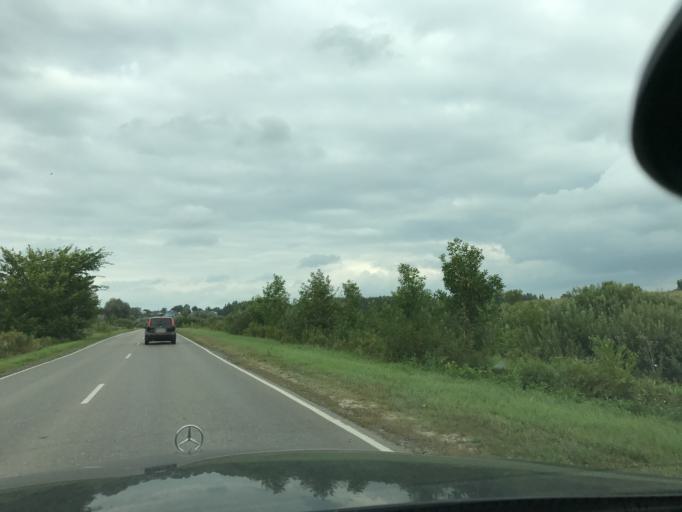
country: RU
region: Nizjnij Novgorod
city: Pavlovo
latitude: 55.9845
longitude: 43.0467
